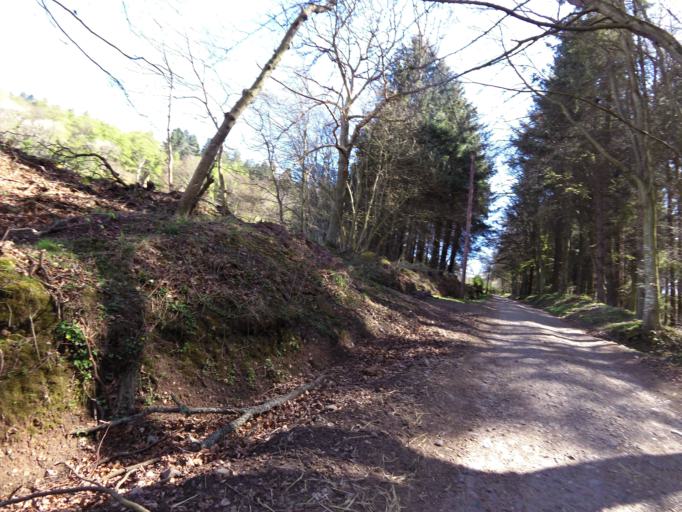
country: GB
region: Scotland
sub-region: Fife
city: Cupar
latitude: 56.3917
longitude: -3.0691
